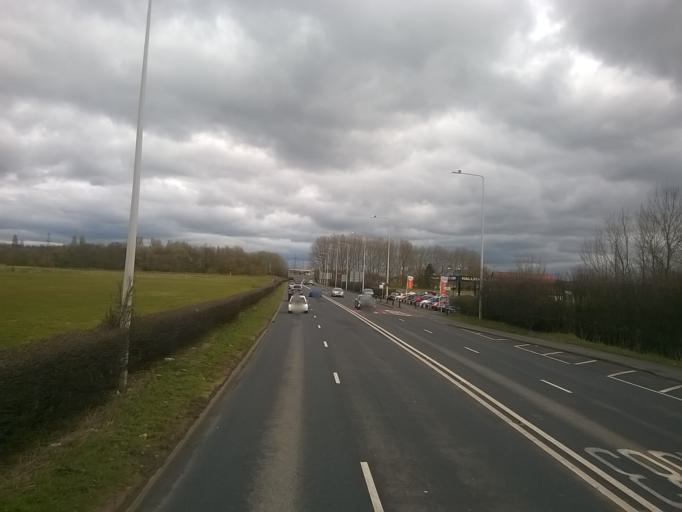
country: GB
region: England
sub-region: Lancashire
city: Freckleton
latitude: 53.7613
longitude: -2.7999
